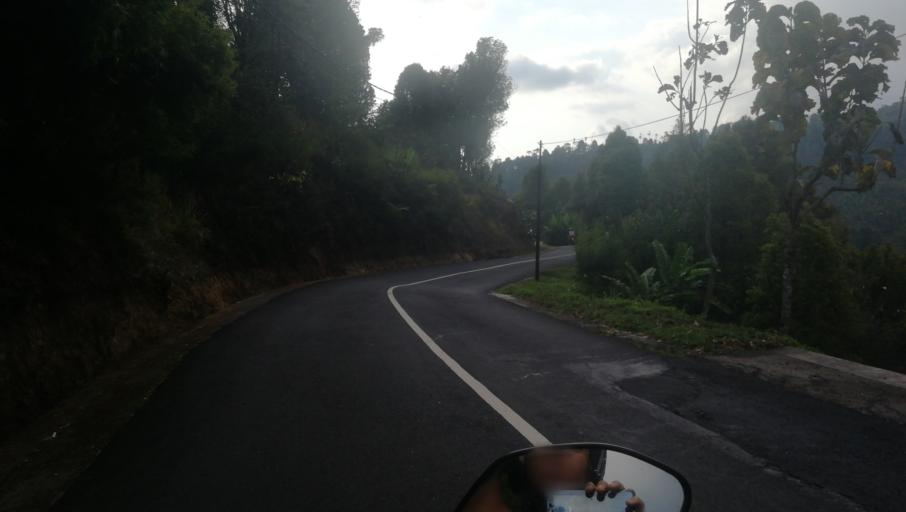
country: ID
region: Bali
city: Munduk
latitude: -8.2542
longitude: 115.0765
